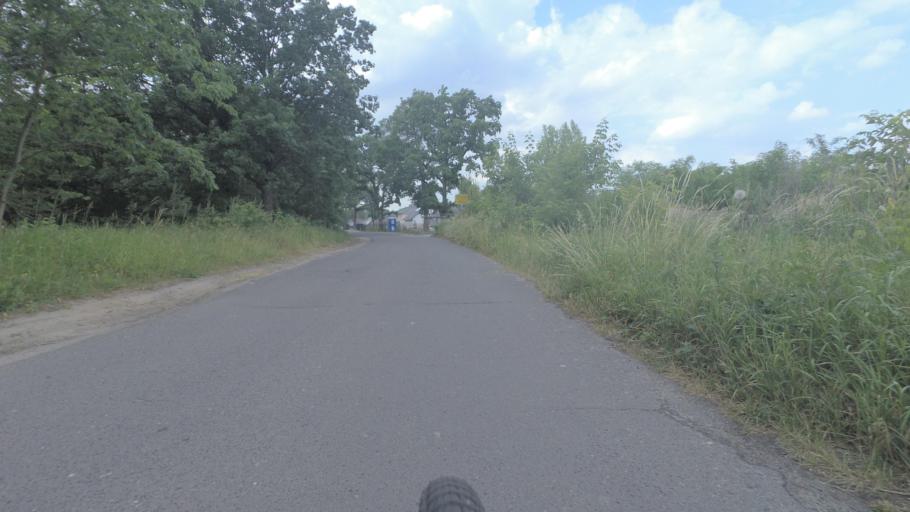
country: DE
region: Brandenburg
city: Zossen
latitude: 52.1883
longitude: 13.4741
